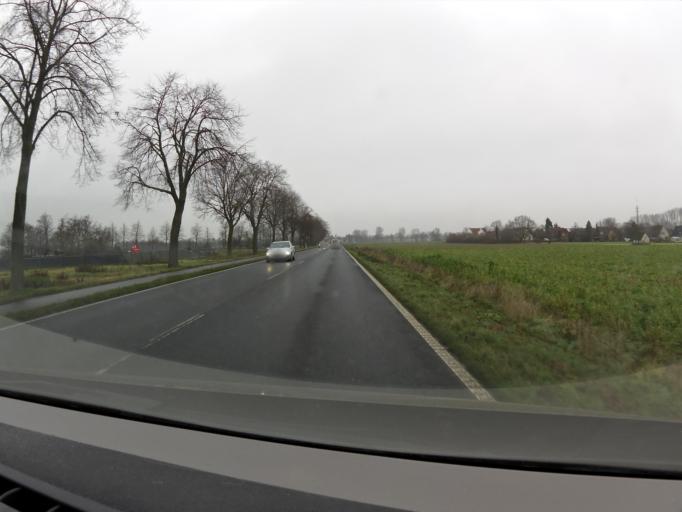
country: DE
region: North Rhine-Westphalia
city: Geldern
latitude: 51.5083
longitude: 6.3064
